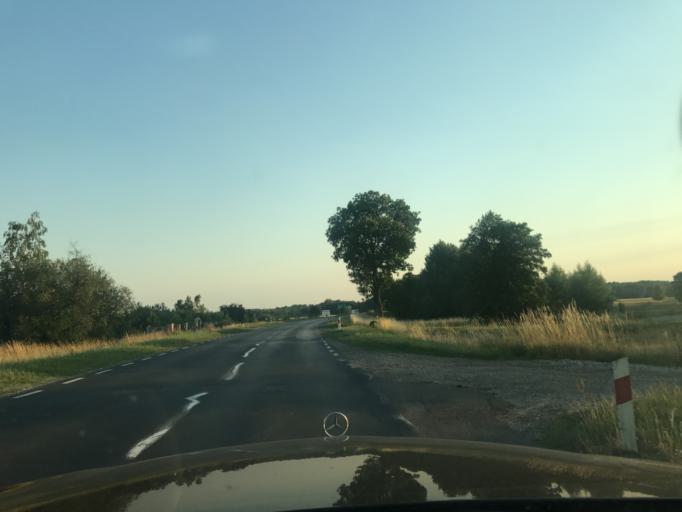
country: PL
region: Lublin Voivodeship
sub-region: Powiat lubartowski
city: Lubartow
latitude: 51.4831
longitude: 22.6246
